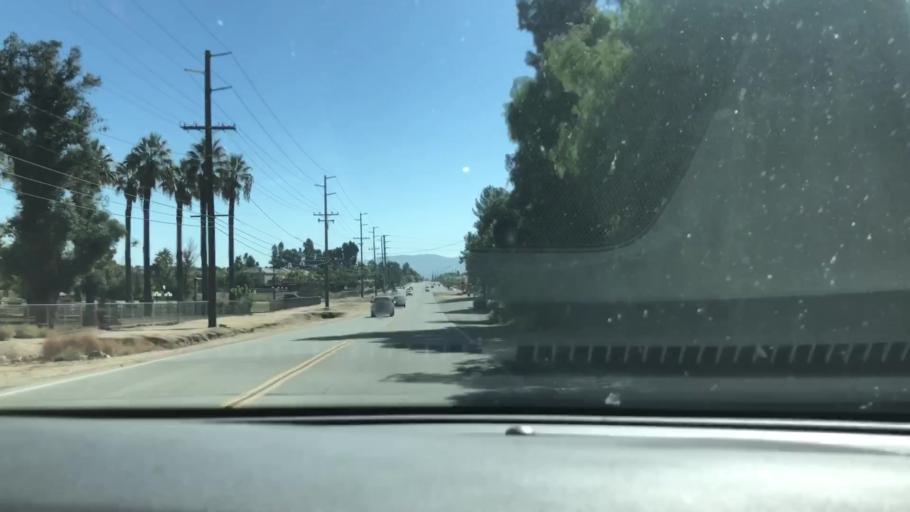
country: US
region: California
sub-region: Riverside County
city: Wildomar
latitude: 33.5985
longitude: -117.2651
